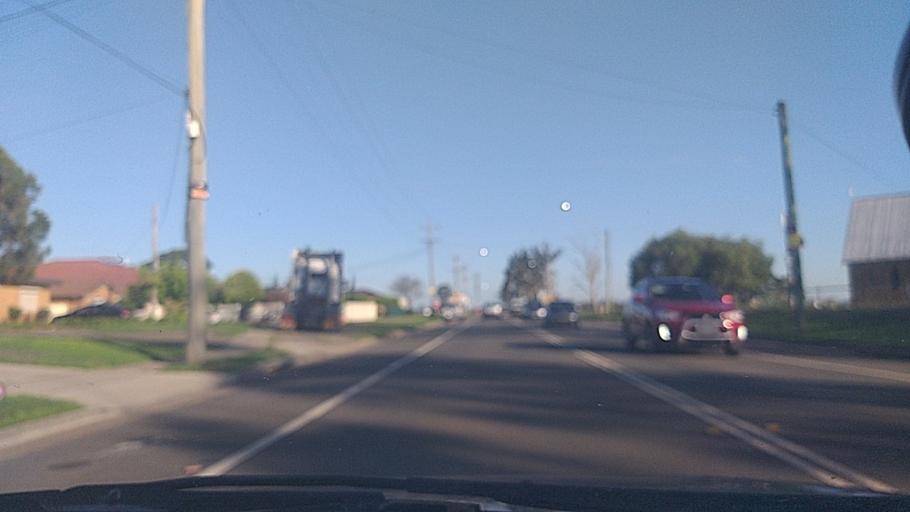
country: AU
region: New South Wales
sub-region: Liverpool
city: Luddenham
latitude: -33.8823
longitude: 150.6915
